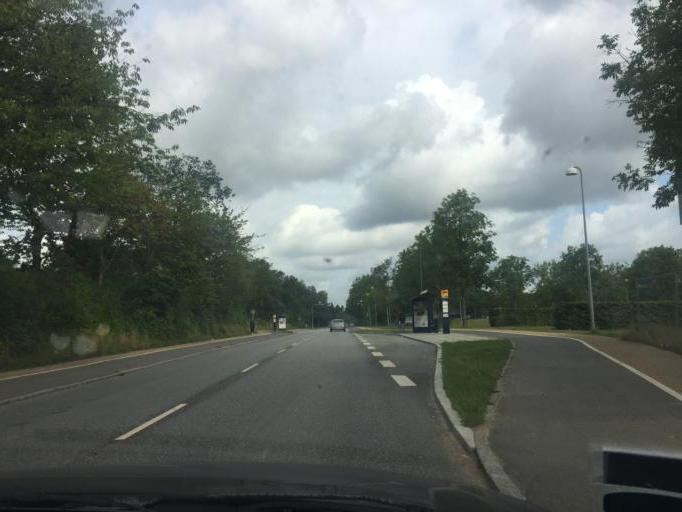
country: DK
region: Capital Region
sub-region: Allerod Kommune
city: Lillerod
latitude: 55.8762
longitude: 12.3529
